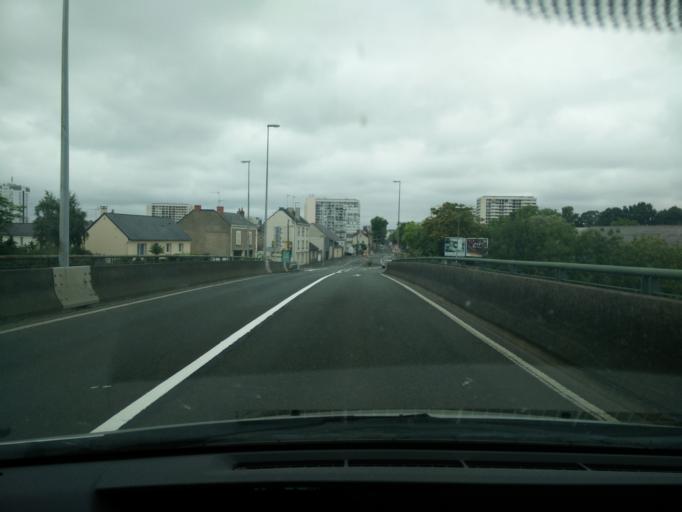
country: FR
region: Pays de la Loire
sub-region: Departement de Maine-et-Loire
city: Angers
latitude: 47.4679
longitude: -0.5294
